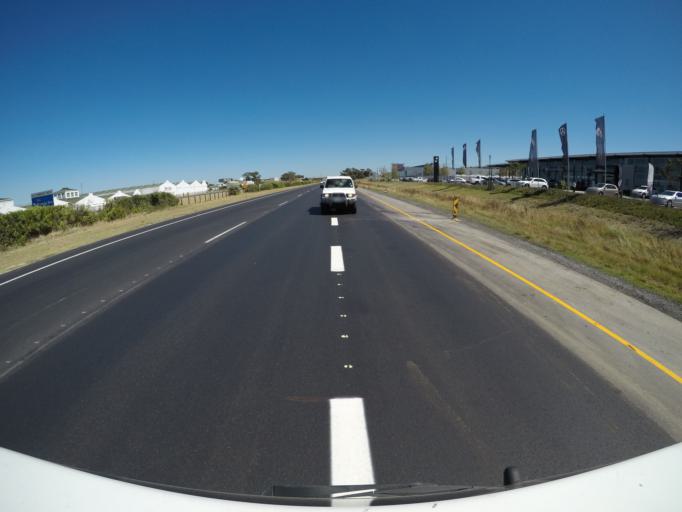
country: ZA
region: Western Cape
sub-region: Cape Winelands District Municipality
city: Stellenbosch
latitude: -34.0802
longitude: 18.8247
